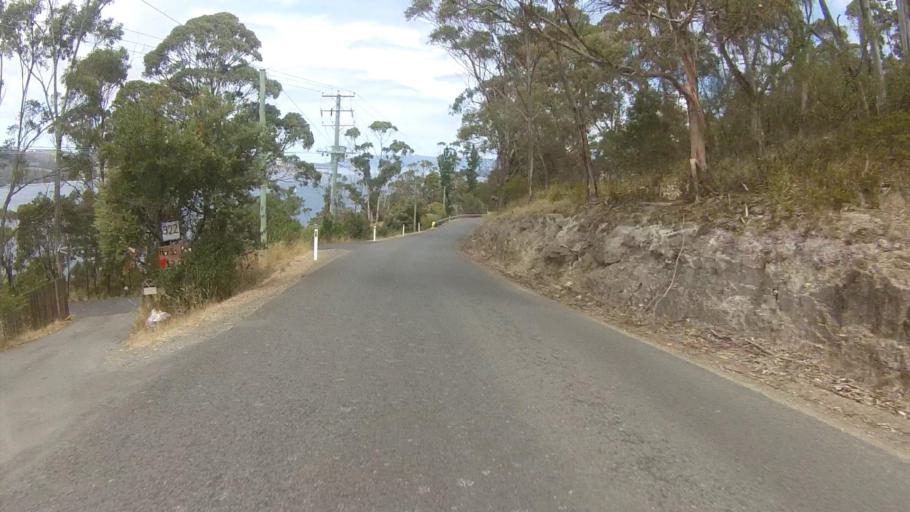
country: AU
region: Tasmania
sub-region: Kingborough
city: Blackmans Bay
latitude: -43.0529
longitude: 147.3385
